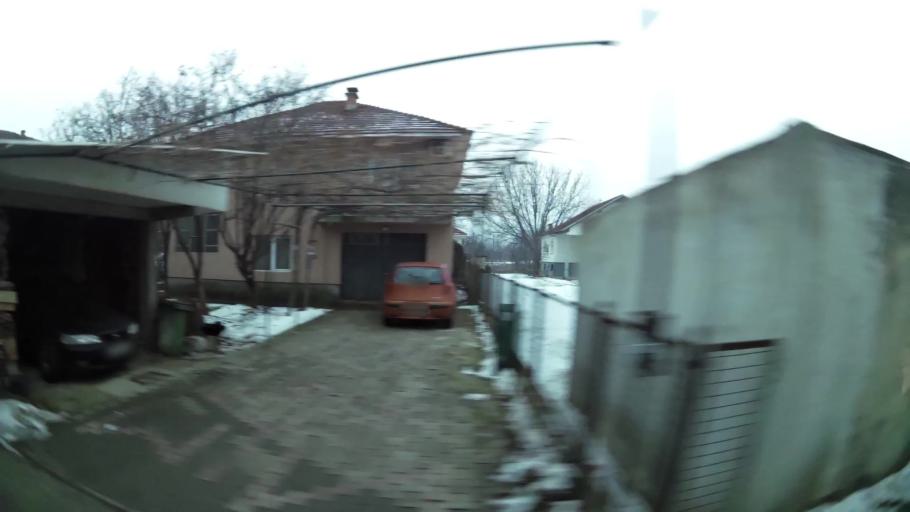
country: MK
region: Kisela Voda
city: Usje
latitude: 41.9698
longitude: 21.4760
